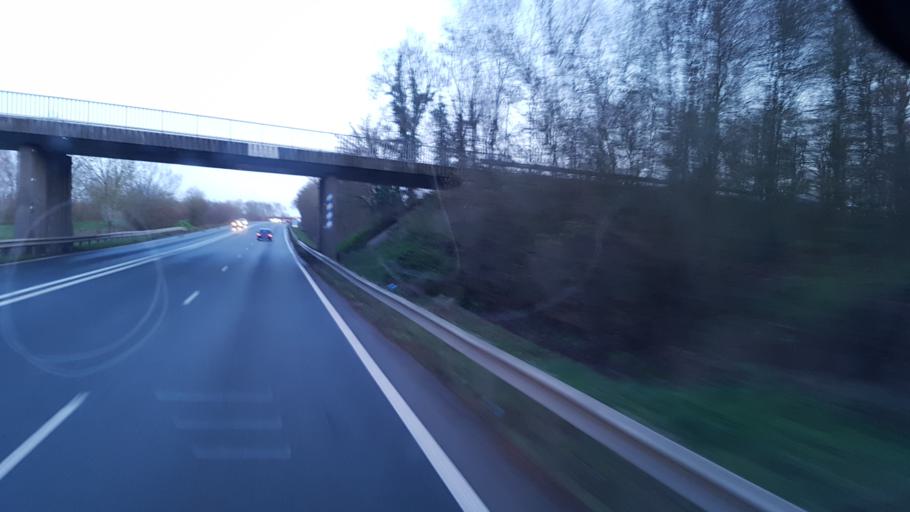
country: FR
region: Nord-Pas-de-Calais
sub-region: Departement du Nord
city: Lambres-lez-Douai
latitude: 50.3460
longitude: 3.0712
